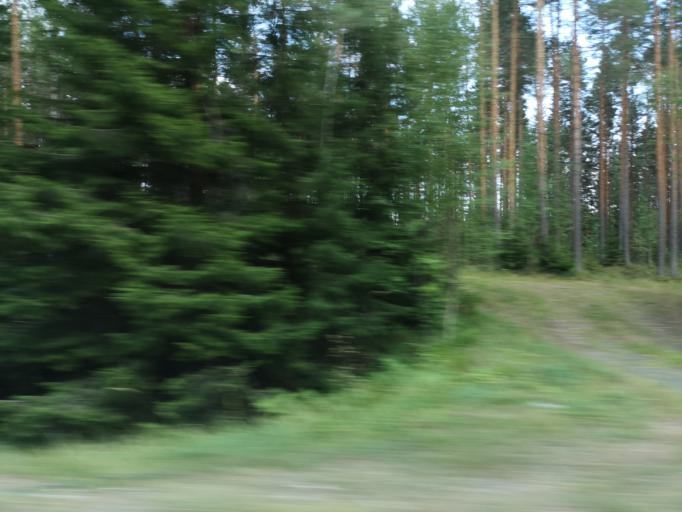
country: FI
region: Paijanne Tavastia
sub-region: Lahti
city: Hartola
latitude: 61.6635
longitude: 26.0322
